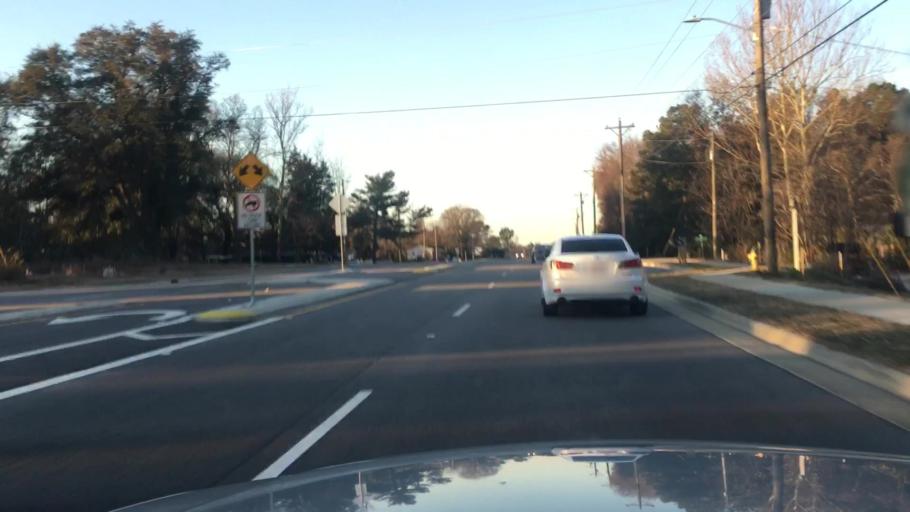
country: US
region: North Carolina
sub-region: Cumberland County
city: Hope Mills
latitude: 35.0045
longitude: -78.9233
